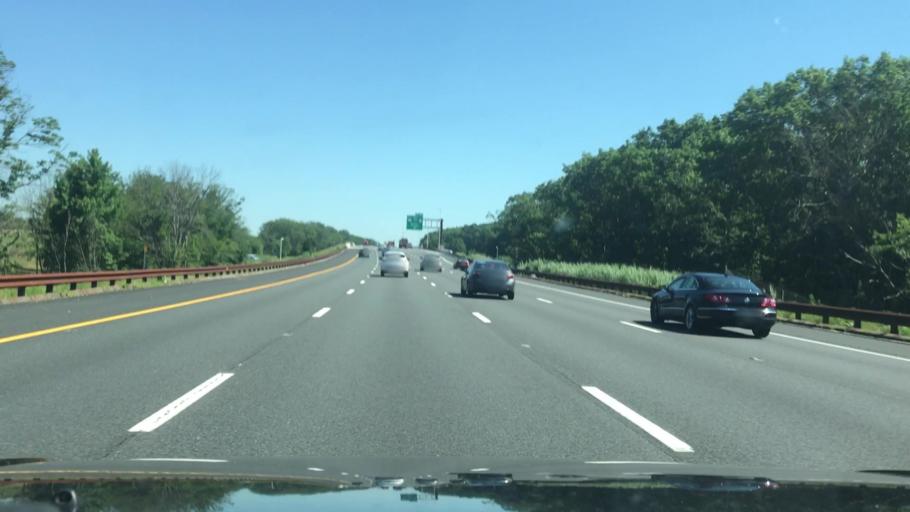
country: US
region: New Jersey
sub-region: Monmouth County
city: Ramtown
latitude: 40.1582
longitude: -74.1027
